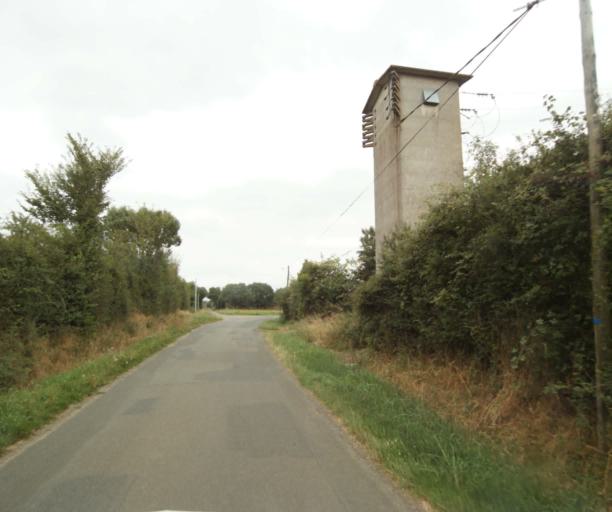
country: FR
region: Pays de la Loire
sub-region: Departement de la Sarthe
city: Juigne-sur-Sarthe
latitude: 47.8475
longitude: -0.2751
